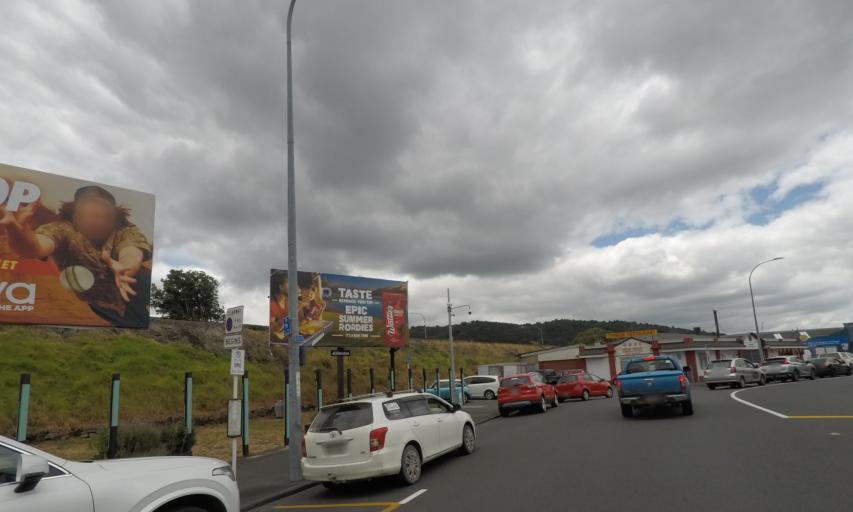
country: NZ
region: Northland
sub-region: Whangarei
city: Whangarei
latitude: -35.7267
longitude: 174.3192
